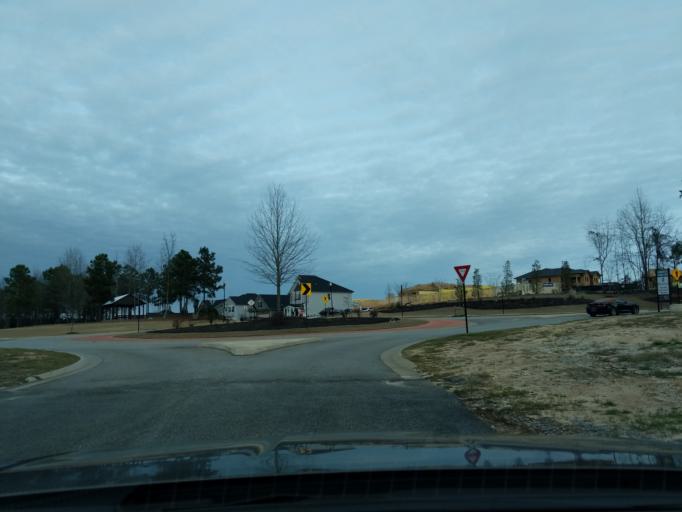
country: US
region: Georgia
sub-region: Columbia County
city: Grovetown
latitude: 33.4666
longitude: -82.2007
